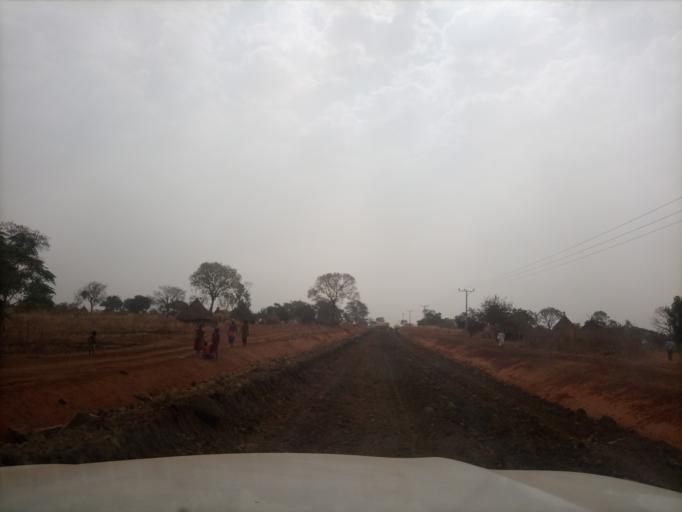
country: ET
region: Oromiya
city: Mendi
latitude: 10.1282
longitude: 35.1315
